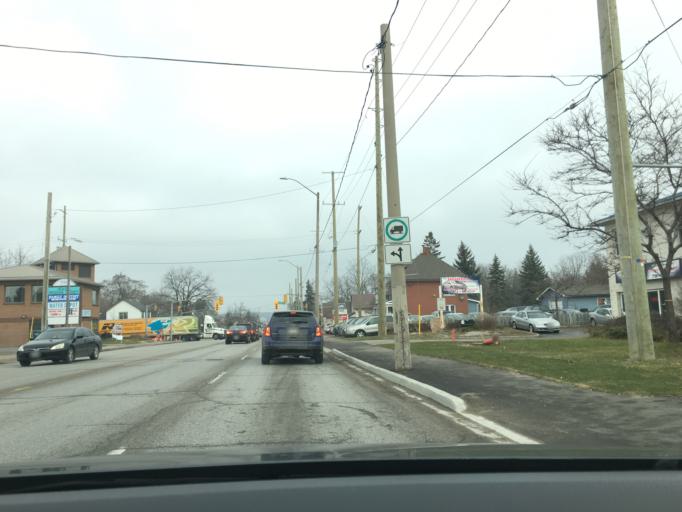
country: CA
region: Ontario
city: Barrie
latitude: 44.3674
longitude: -79.6953
